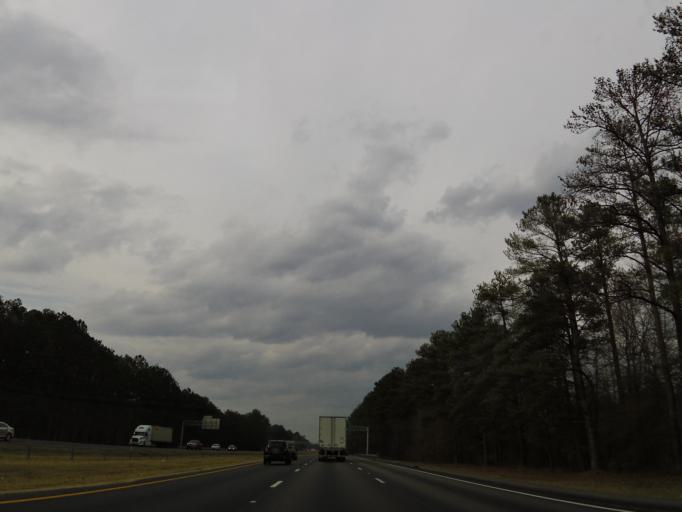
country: US
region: South Carolina
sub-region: Lexington County
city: Pineridge
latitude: 33.8957
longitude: -81.0445
